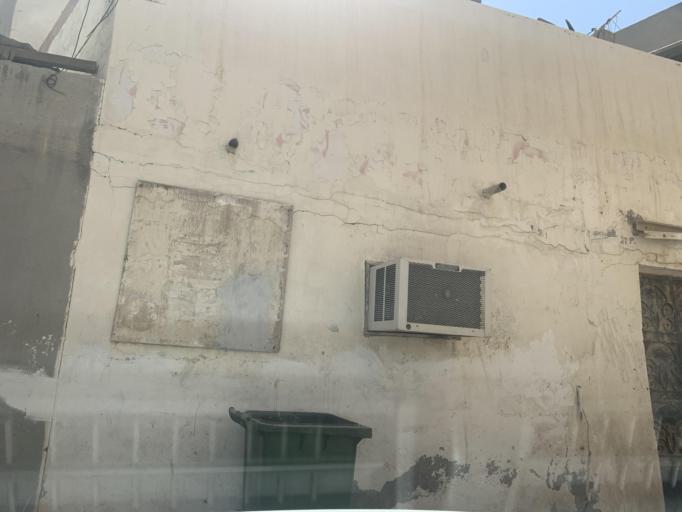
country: BH
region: Manama
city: Jidd Hafs
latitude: 26.2180
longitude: 50.5335
